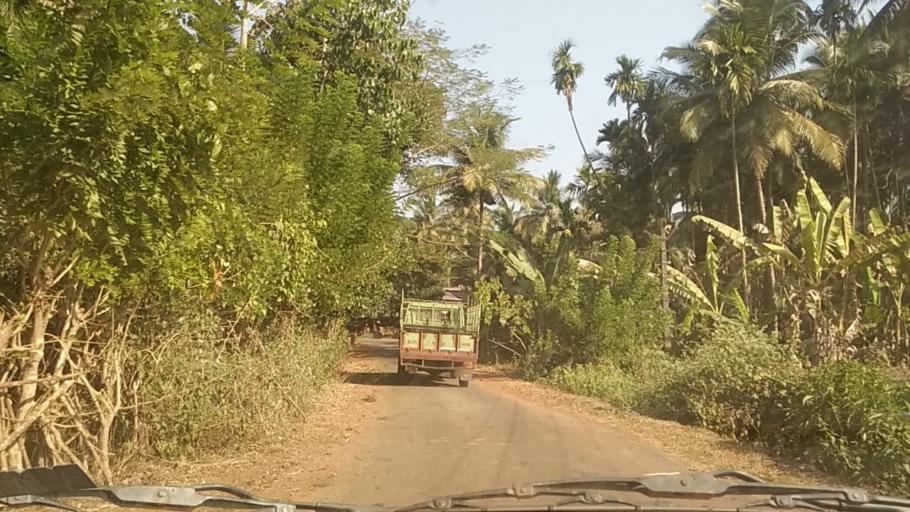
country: IN
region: Goa
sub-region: North Goa
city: Ponda
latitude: 15.4007
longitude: 74.0663
